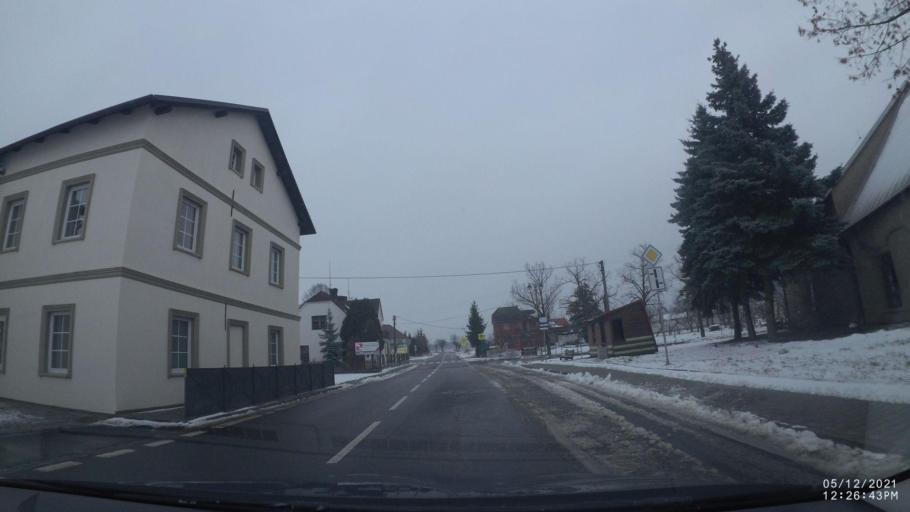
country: CZ
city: Nove Mesto nad Metuji
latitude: 50.3328
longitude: 16.1051
